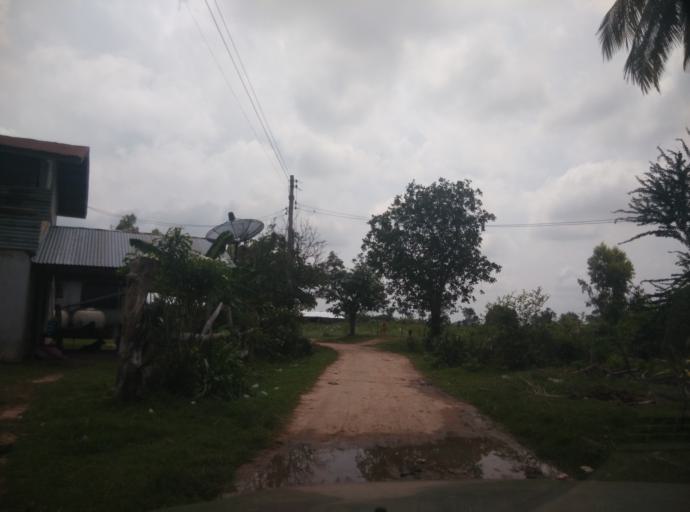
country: TH
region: Sisaket
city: Prang Ku
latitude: 14.9494
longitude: 104.0696
